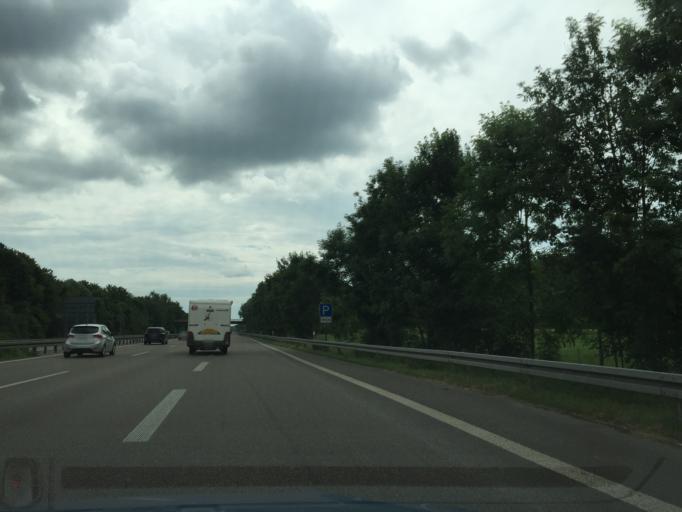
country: DE
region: Bavaria
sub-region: Swabia
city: Neu-Ulm
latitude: 48.3666
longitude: 9.9998
